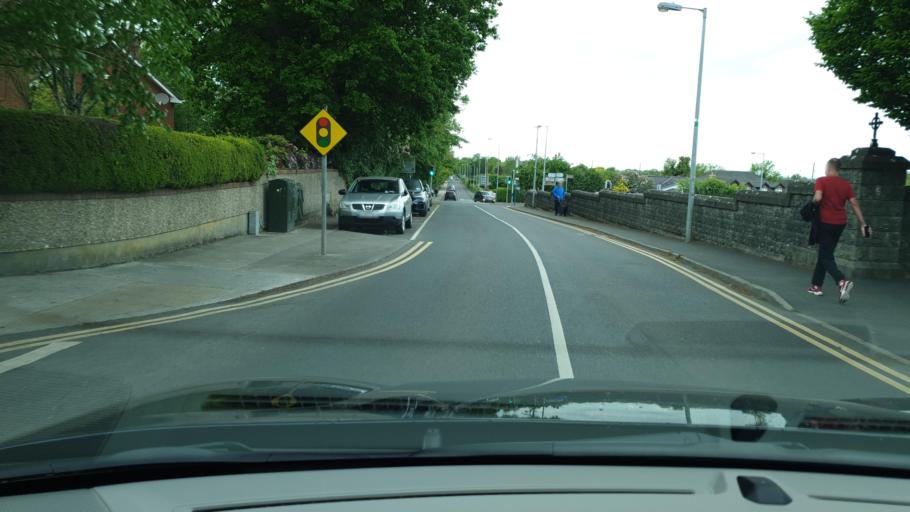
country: IE
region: Leinster
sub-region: An Mhi
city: Ratoath
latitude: 53.5086
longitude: -6.4618
